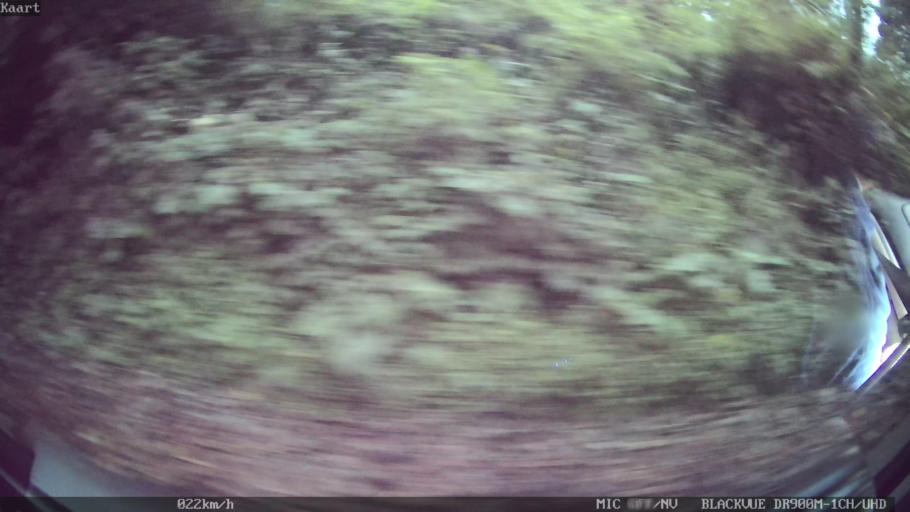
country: ID
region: Bali
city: Peneng
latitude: -8.3693
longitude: 115.2155
